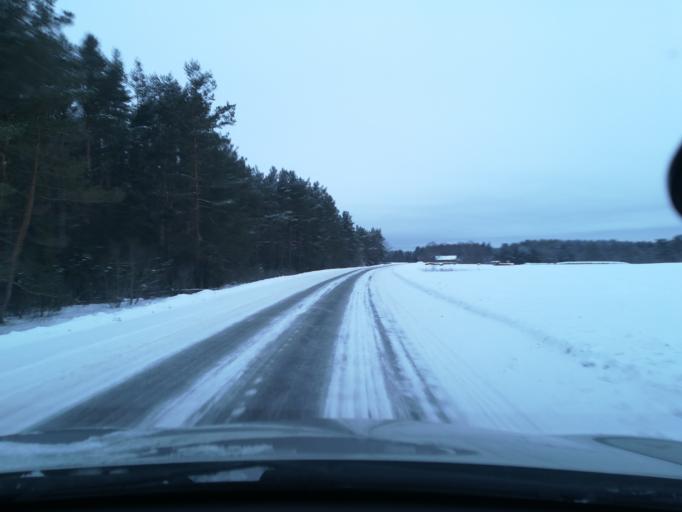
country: EE
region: Harju
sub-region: Keila linn
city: Keila
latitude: 59.3582
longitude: 24.3401
